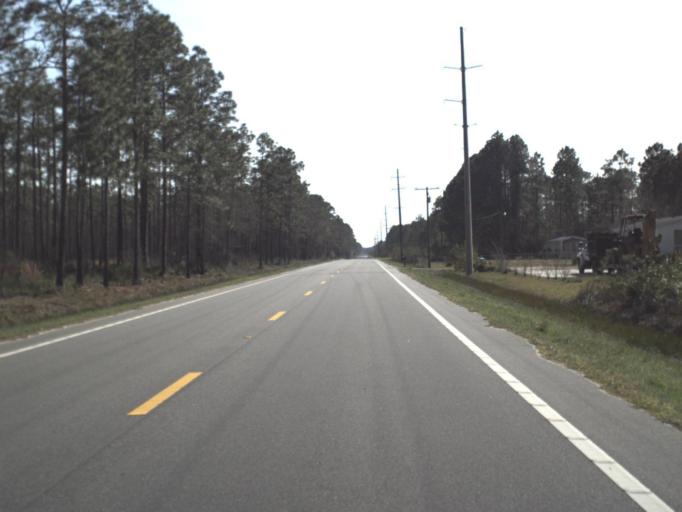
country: US
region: Florida
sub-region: Wakulla County
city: Crawfordville
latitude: 30.0352
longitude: -84.4968
